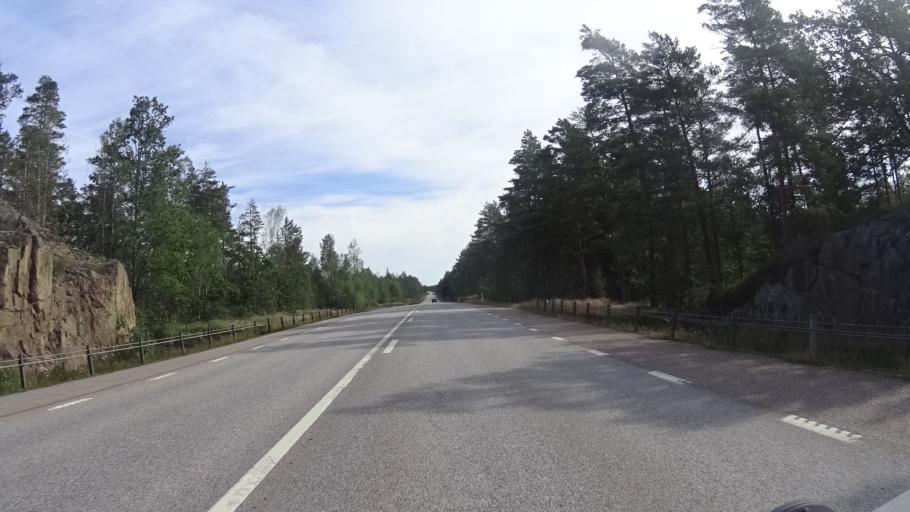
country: SE
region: Kalmar
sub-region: Oskarshamns Kommun
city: Oskarshamn
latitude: 57.4462
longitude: 16.5011
